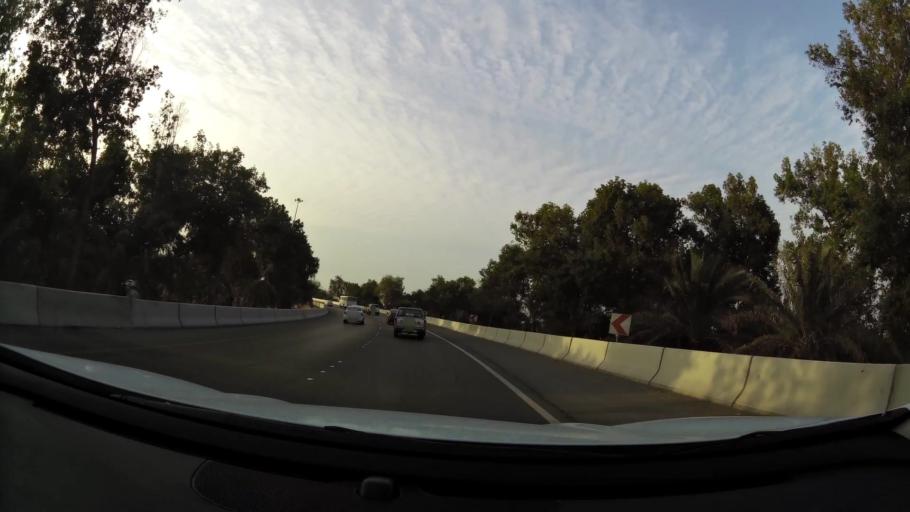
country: AE
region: Abu Dhabi
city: Abu Dhabi
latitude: 24.3933
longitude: 54.5266
